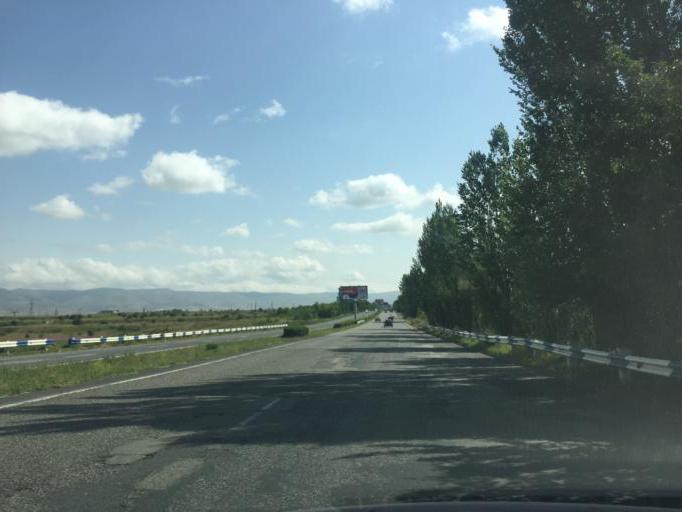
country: AM
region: Kotayk'i Marz
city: Hrazdan
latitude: 40.5014
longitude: 44.7912
